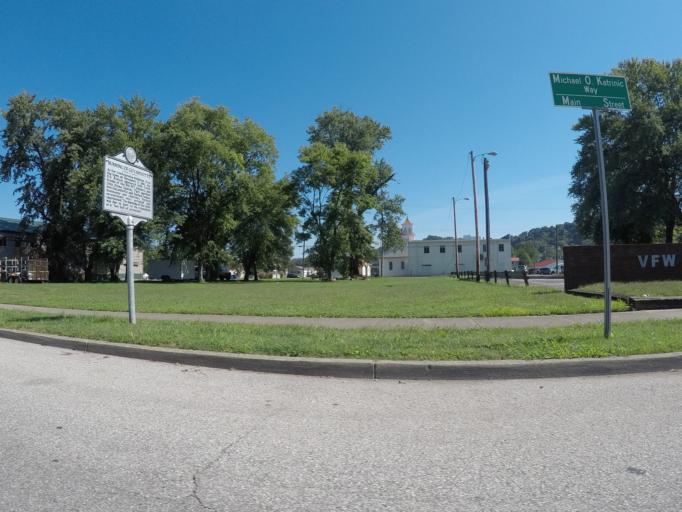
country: US
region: West Virginia
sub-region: Cabell County
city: Huntington
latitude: 38.4288
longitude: -82.3888
